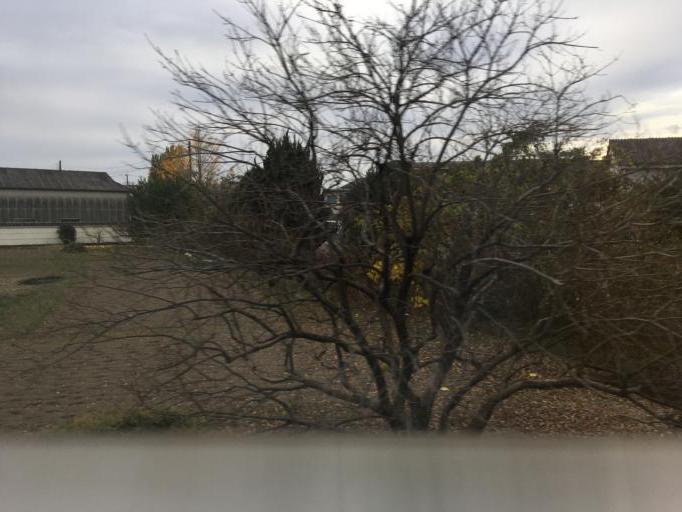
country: JP
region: Tochigi
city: Tochigi
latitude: 36.3640
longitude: 139.7566
